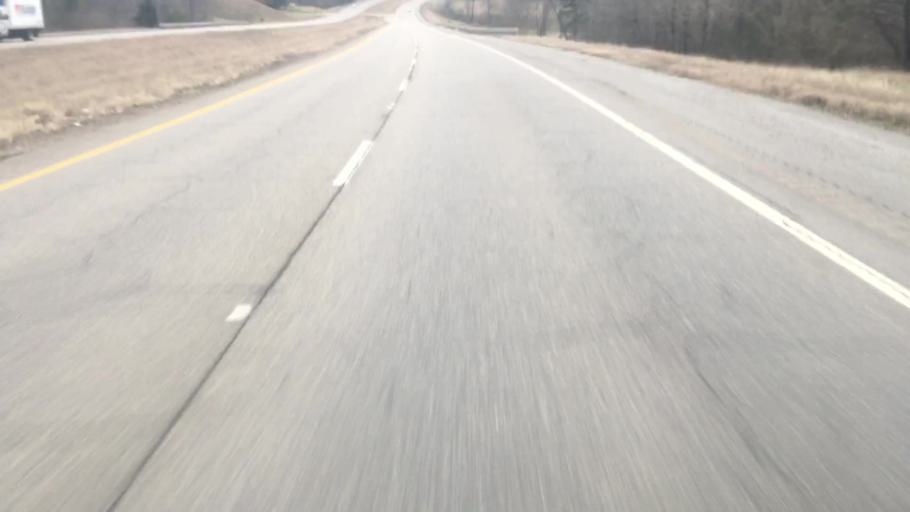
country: US
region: Alabama
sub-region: Walker County
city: Sumiton
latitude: 33.7944
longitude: -87.1049
